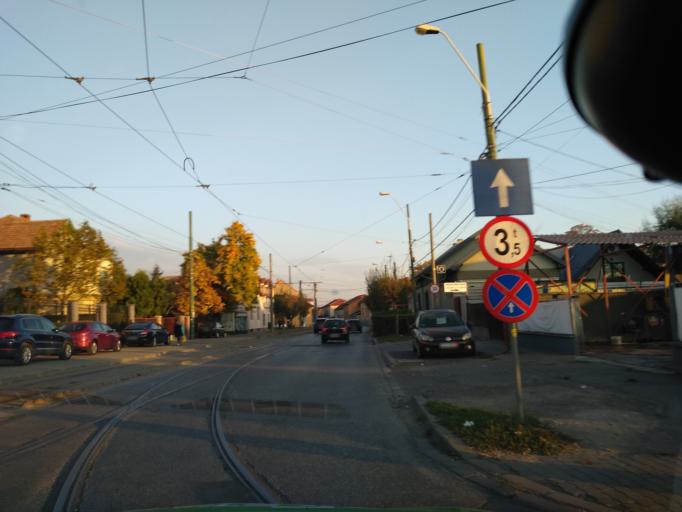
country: RO
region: Timis
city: Timisoara
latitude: 45.7352
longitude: 21.2267
